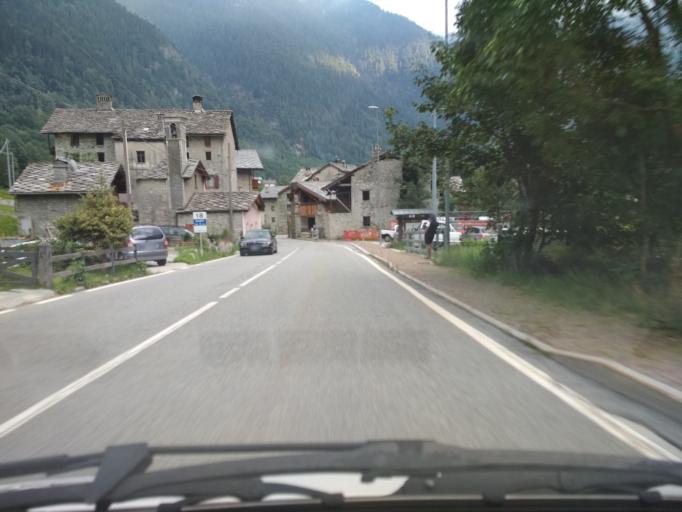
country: IT
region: Aosta Valley
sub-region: Valle d'Aosta
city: Gaby
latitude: 45.7176
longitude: 7.8794
